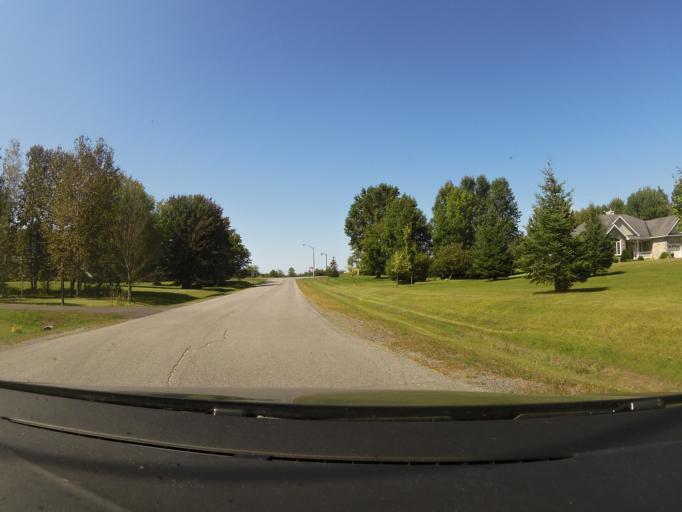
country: CA
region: Ontario
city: Bells Corners
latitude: 45.2857
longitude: -75.9983
